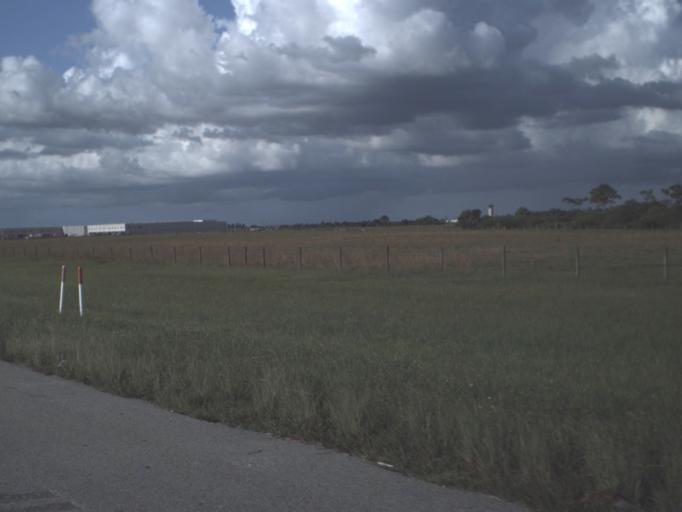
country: US
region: Florida
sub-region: Charlotte County
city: Charlotte Park
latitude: 26.9002
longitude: -82.0067
